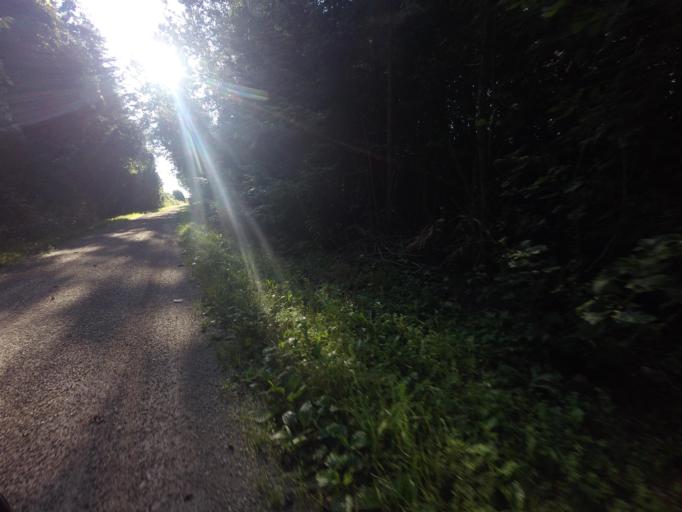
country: CA
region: Ontario
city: Goderich
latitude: 43.7642
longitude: -81.5312
